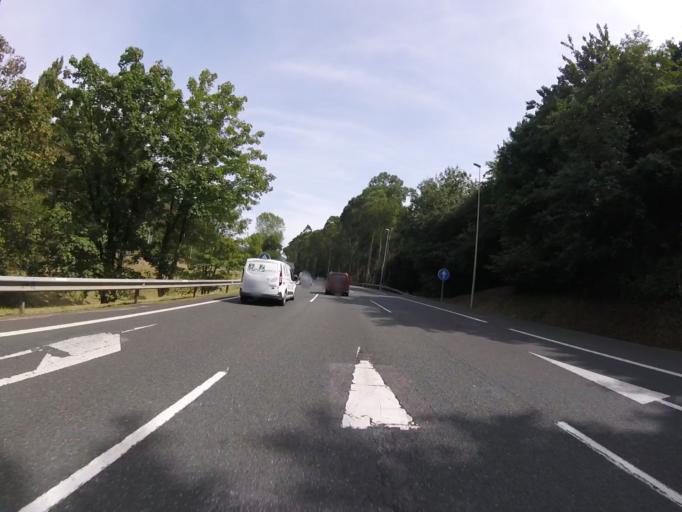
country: ES
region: Basque Country
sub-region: Provincia de Guipuzcoa
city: San Sebastian
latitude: 43.3145
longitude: -1.9541
